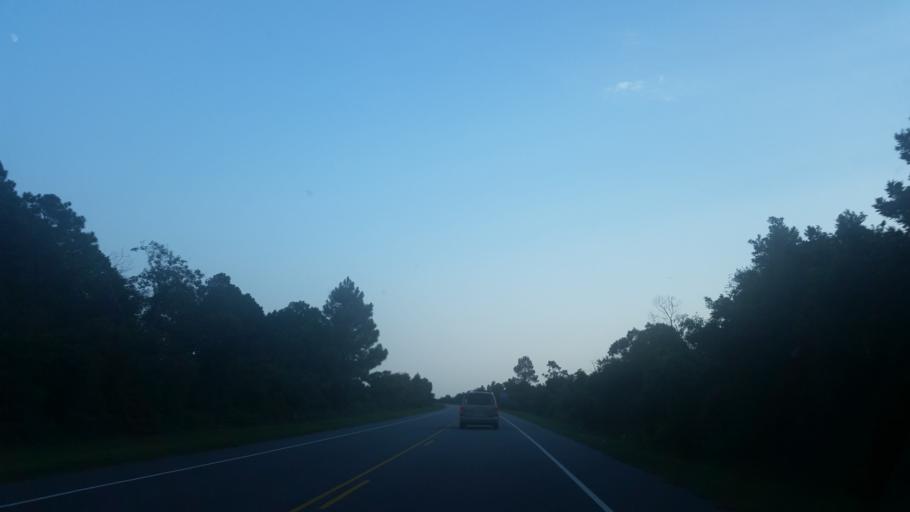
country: US
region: North Carolina
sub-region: Dare County
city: Nags Head
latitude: 35.8993
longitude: -75.5961
